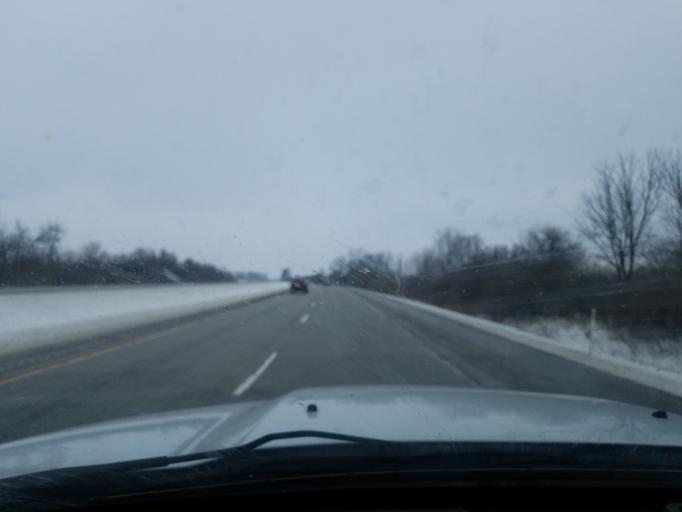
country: US
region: Indiana
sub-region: Marshall County
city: Argos
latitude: 41.1656
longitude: -86.2397
